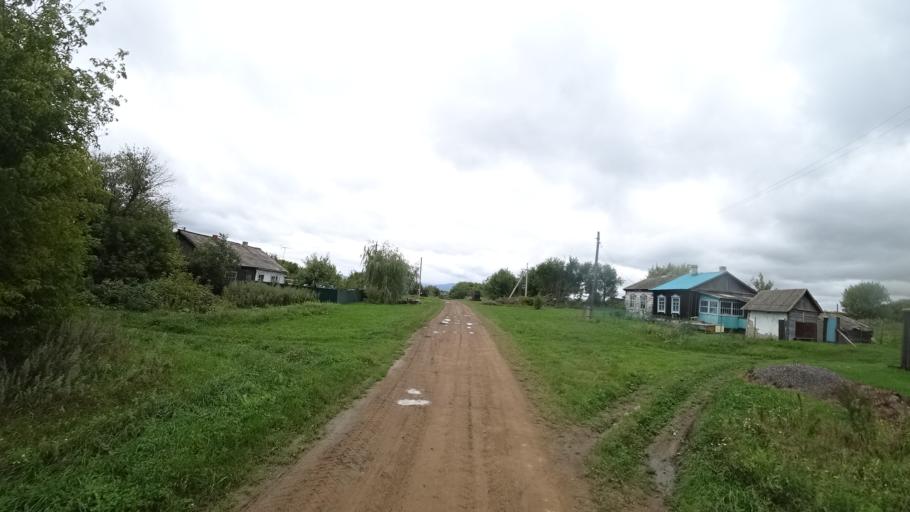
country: RU
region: Primorskiy
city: Chernigovka
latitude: 44.4329
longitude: 132.5921
